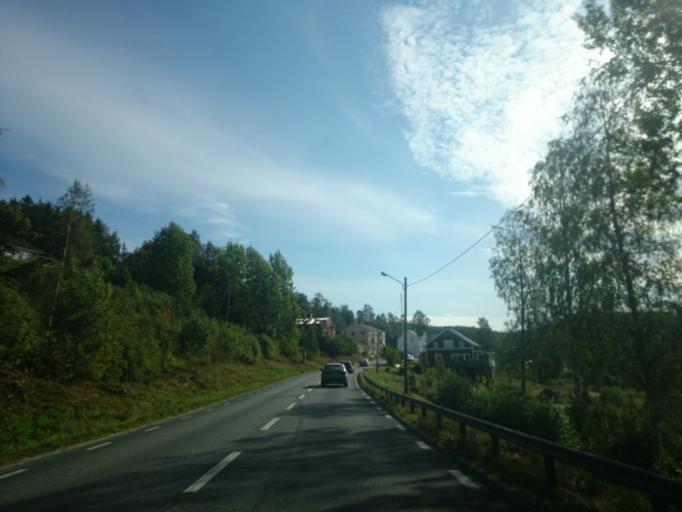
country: SE
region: Vaesternorrland
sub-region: Kramfors Kommun
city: Nordingra
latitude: 62.9297
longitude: 18.2801
